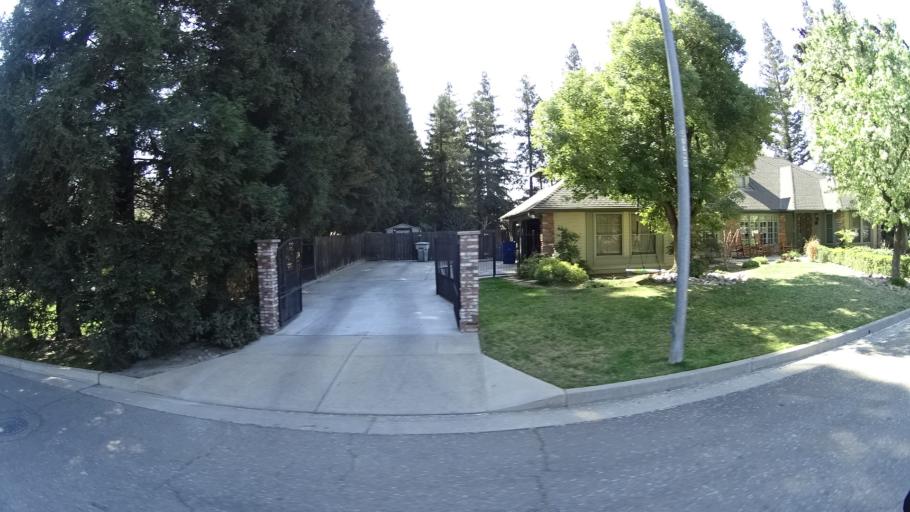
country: US
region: California
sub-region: Fresno County
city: Fresno
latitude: 36.8467
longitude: -119.8214
